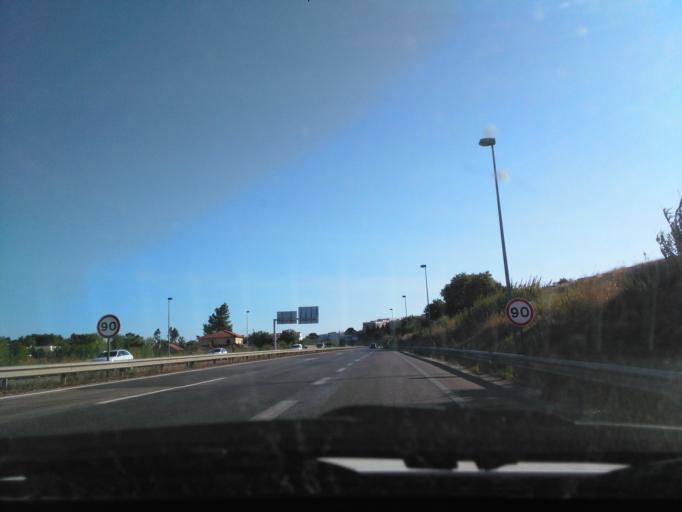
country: PT
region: Santarem
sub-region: Santarem
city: Santarem
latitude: 39.2412
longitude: -8.6990
